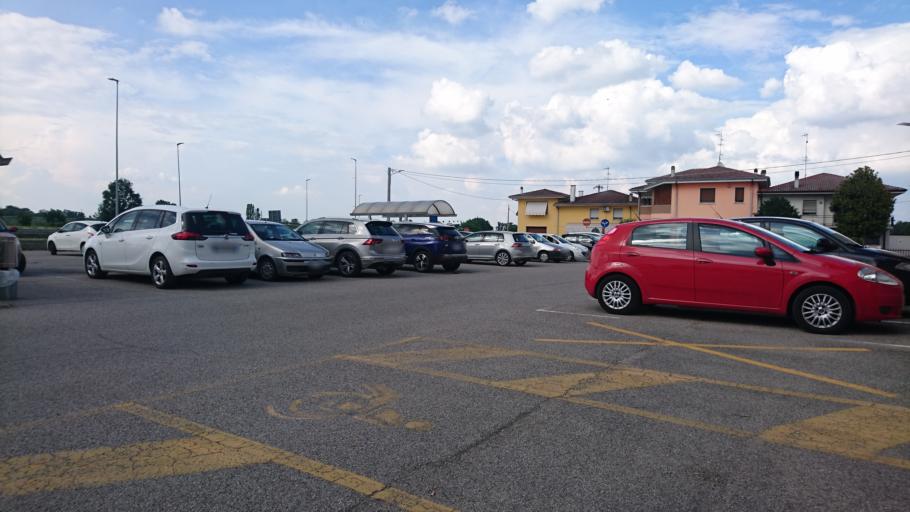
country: IT
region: Lombardy
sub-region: Provincia di Mantova
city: Sermide
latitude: 45.0072
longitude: 11.2867
